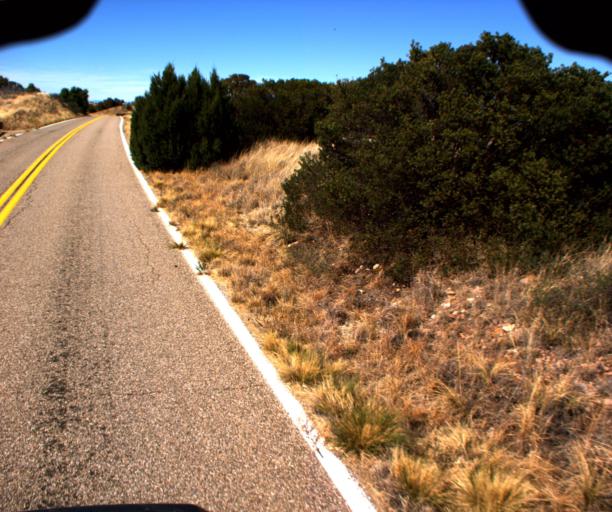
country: US
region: Arizona
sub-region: Cochise County
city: Sierra Vista
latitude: 31.5126
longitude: -110.4969
